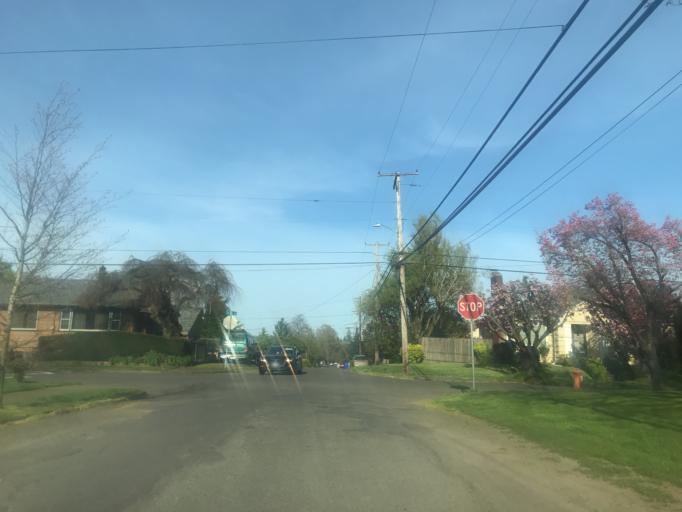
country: US
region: Oregon
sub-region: Multnomah County
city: Lents
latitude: 45.5034
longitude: -122.5824
